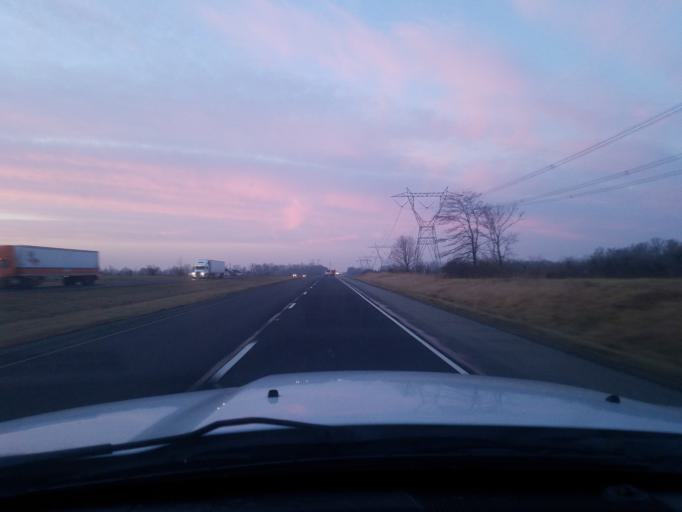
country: US
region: Indiana
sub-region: Huntington County
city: Roanoke
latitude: 40.9272
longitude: -85.3173
